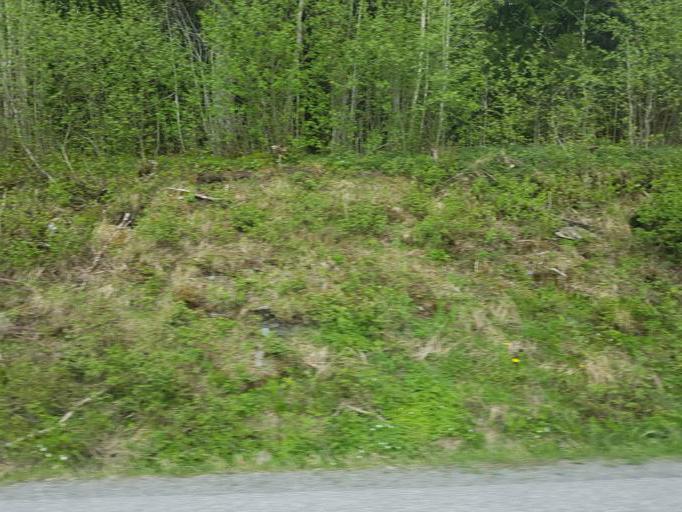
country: NO
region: Nord-Trondelag
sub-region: Levanger
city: Skogn
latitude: 63.6553
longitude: 11.2385
